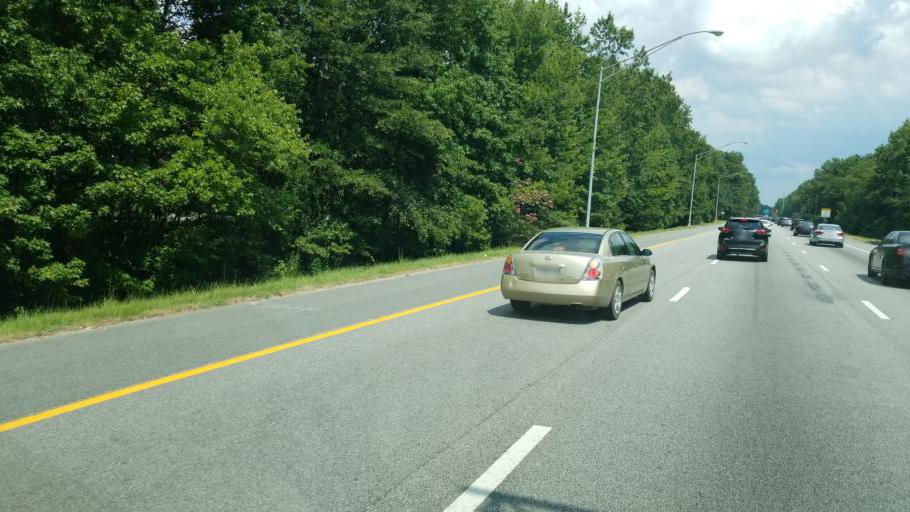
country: US
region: Virginia
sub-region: City of Portsmouth
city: Portsmouth Heights
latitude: 36.7786
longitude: -76.3872
